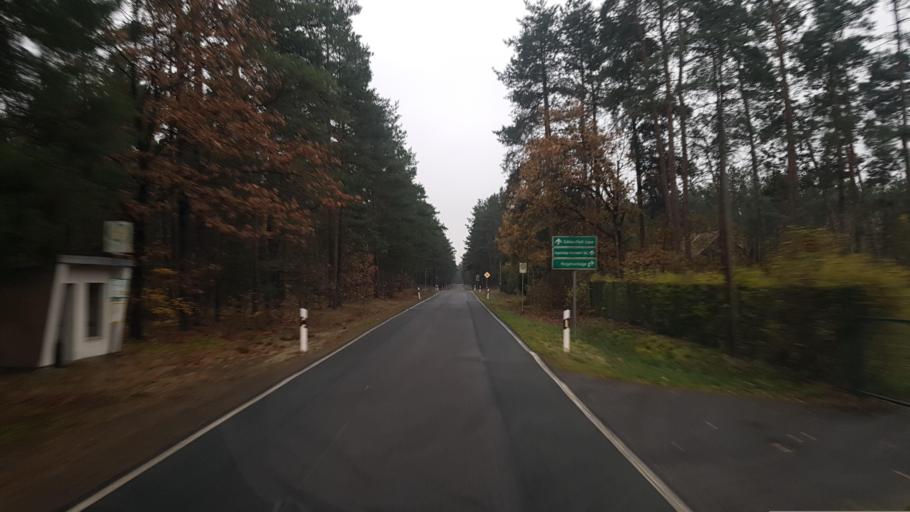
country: DE
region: Brandenburg
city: Ruhland
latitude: 51.4315
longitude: 13.8783
